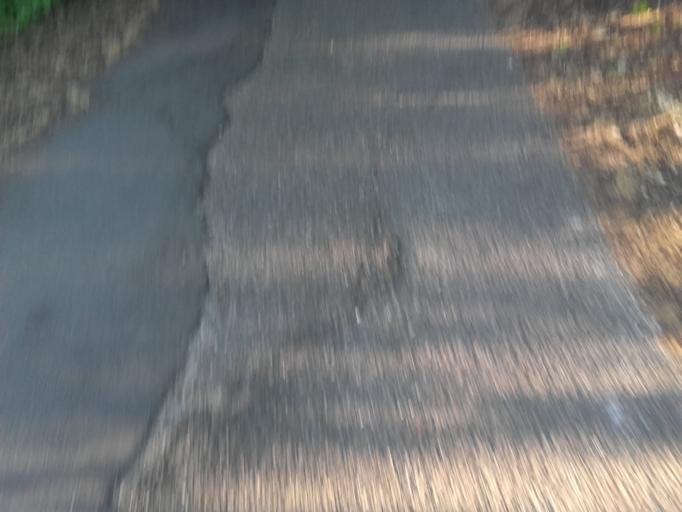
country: FR
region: Aquitaine
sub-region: Departement de la Gironde
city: Cenon
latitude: 44.8565
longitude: -0.5299
